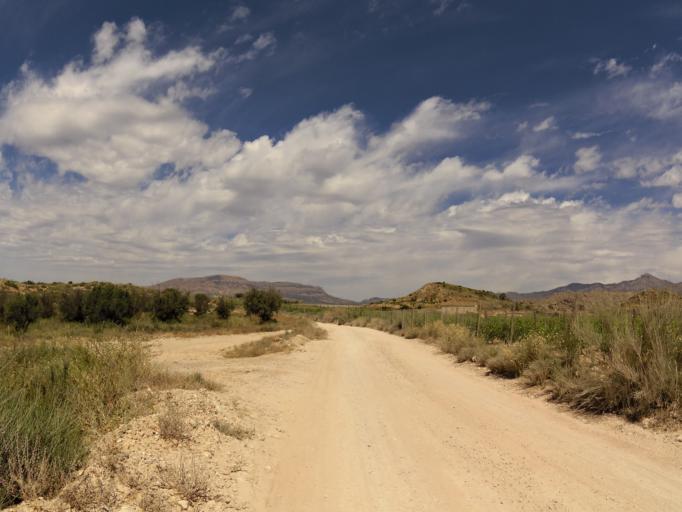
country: ES
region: Valencia
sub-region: Provincia de Alicante
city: Agost
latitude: 38.4053
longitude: -0.6132
